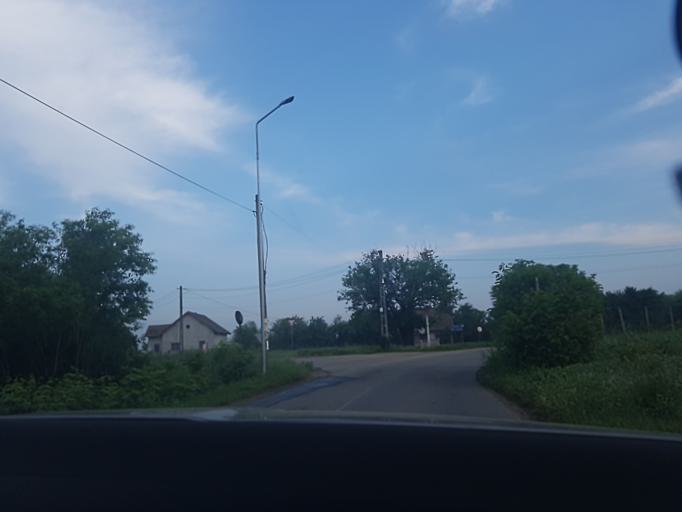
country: RO
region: Timis
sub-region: Comuna Parta
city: Parta
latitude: 45.6442
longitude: 21.1314
